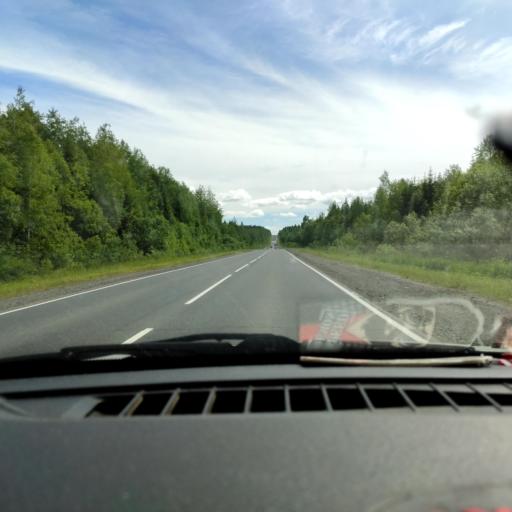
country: RU
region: Perm
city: Chusovoy
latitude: 58.3735
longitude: 57.9809
